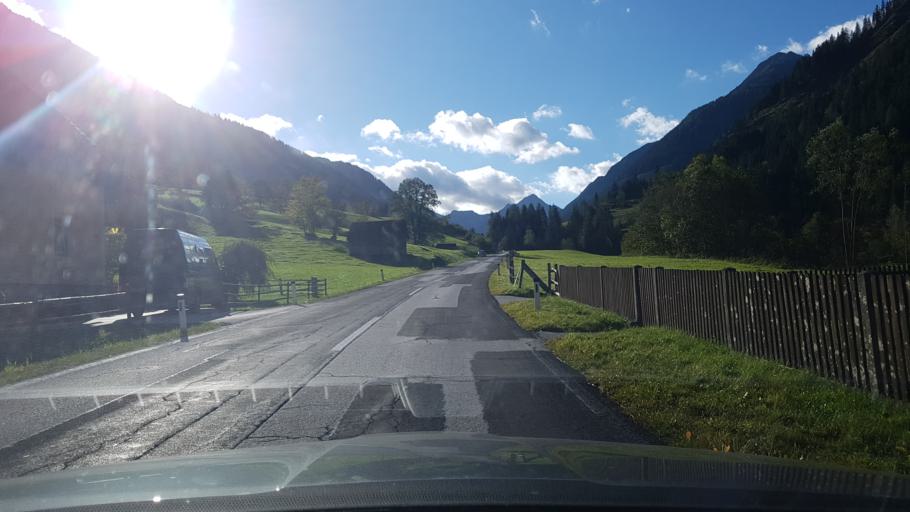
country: AT
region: Styria
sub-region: Politischer Bezirk Liezen
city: Sankt Nikolai im Solktal
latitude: 47.3341
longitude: 14.0399
